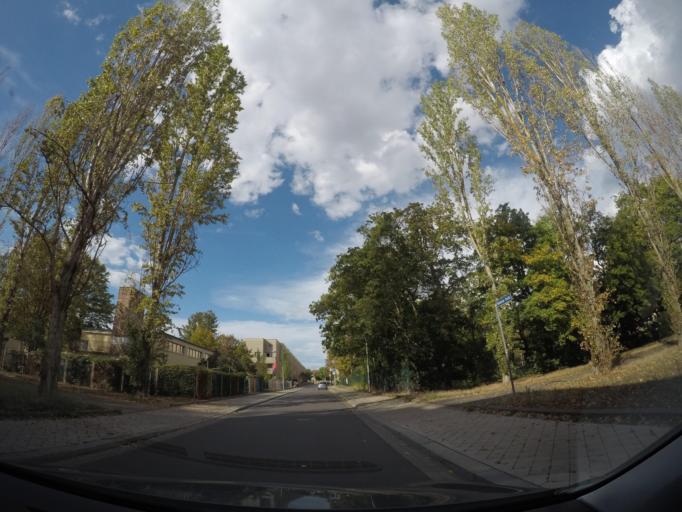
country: DE
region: Saxony-Anhalt
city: Diesdorf
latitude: 52.1267
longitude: 11.5880
